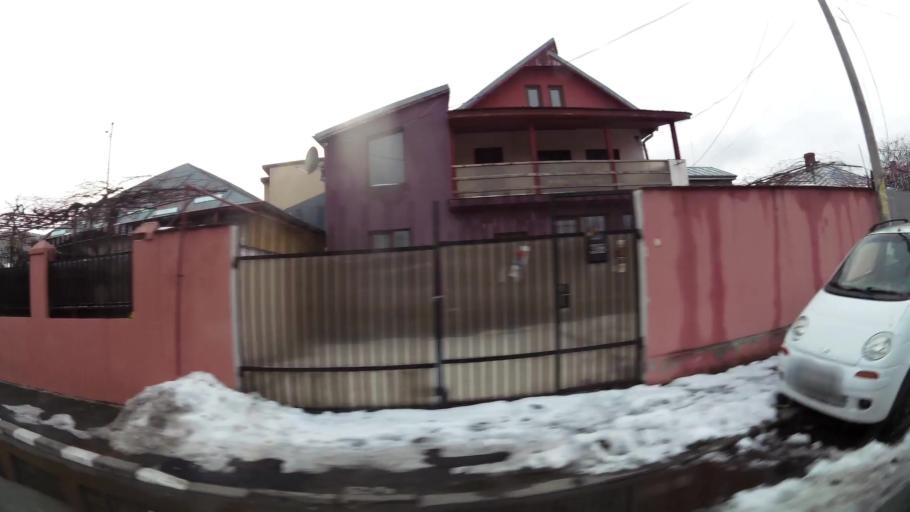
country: RO
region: Ilfov
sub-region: Voluntari City
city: Voluntari
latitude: 44.4759
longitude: 26.1731
